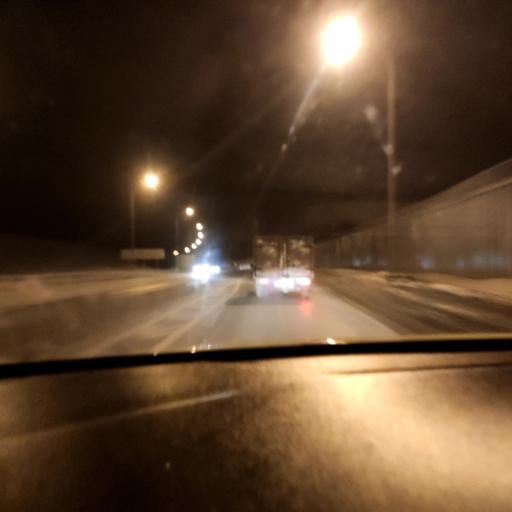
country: RU
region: Tatarstan
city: Aysha
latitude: 55.8735
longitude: 48.6603
